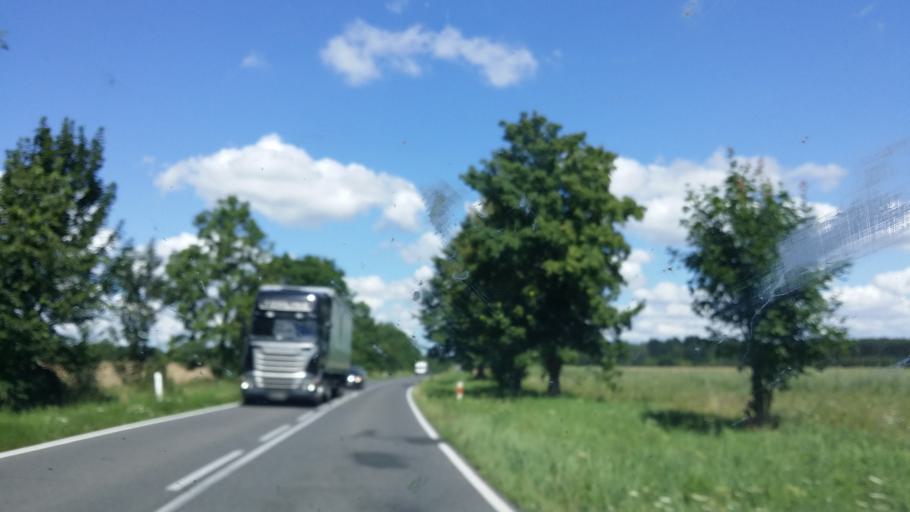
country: PL
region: West Pomeranian Voivodeship
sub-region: Powiat swidwinski
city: Slawoborze
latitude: 53.8482
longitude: 15.7353
